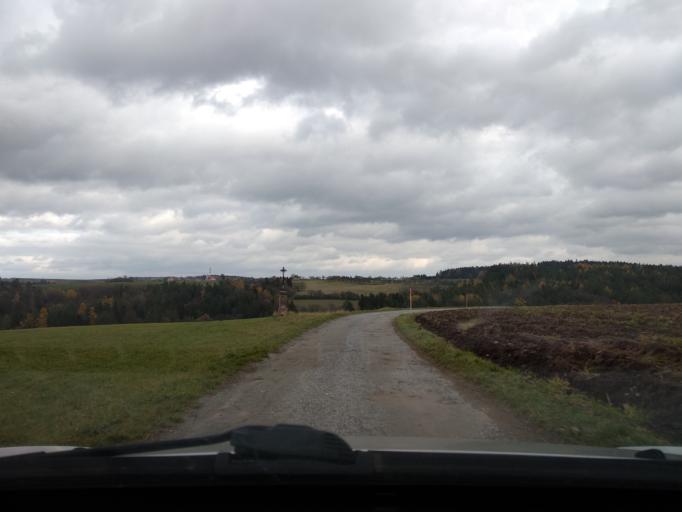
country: CZ
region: South Moravian
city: Drasov
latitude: 49.3739
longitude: 16.4767
